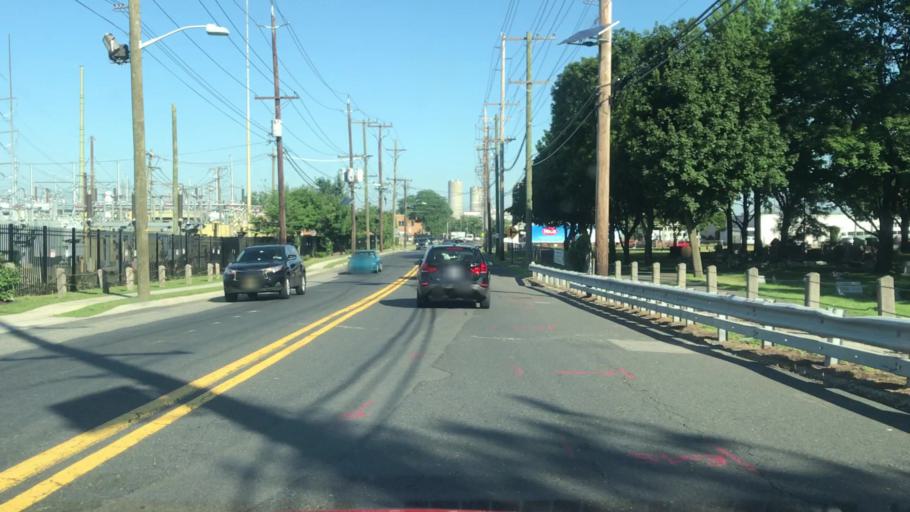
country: US
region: New Jersey
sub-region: Bergen County
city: Ridgefield
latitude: 40.8339
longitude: -74.0139
